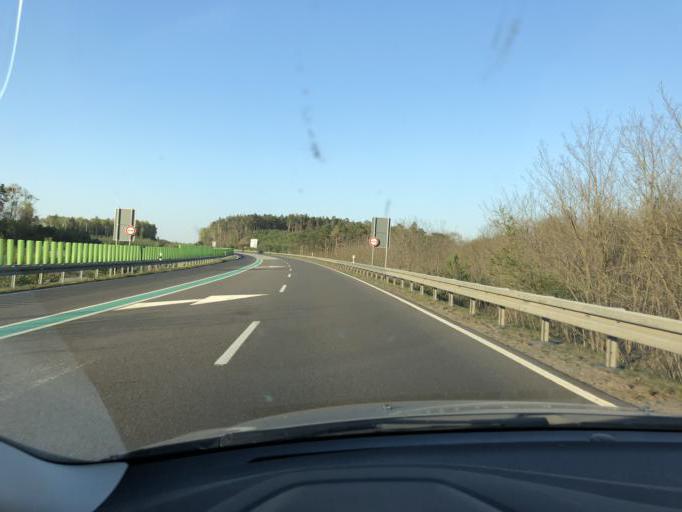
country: DE
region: Brandenburg
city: Schwarzbach
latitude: 51.4890
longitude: 13.9384
